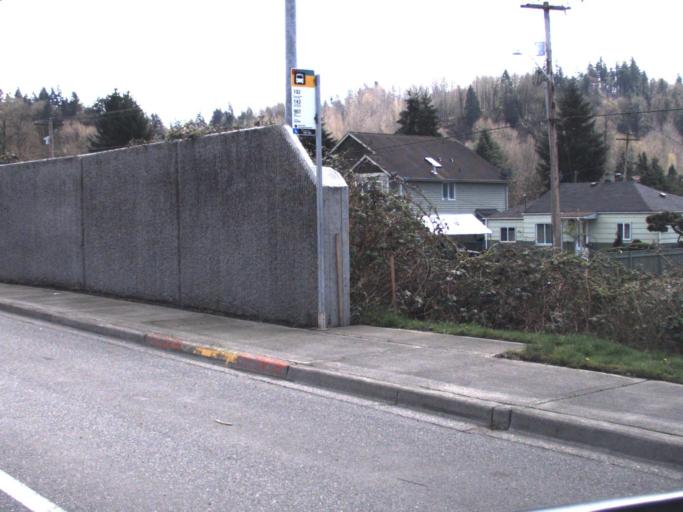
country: US
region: Washington
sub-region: King County
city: Fairwood
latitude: 47.4706
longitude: -122.1624
